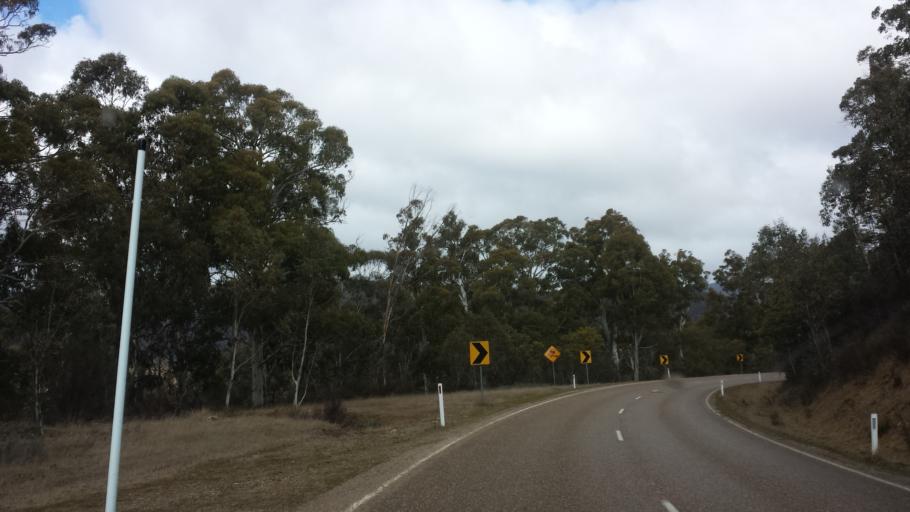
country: AU
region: Victoria
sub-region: Alpine
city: Mount Beauty
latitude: -37.0886
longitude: 147.3844
